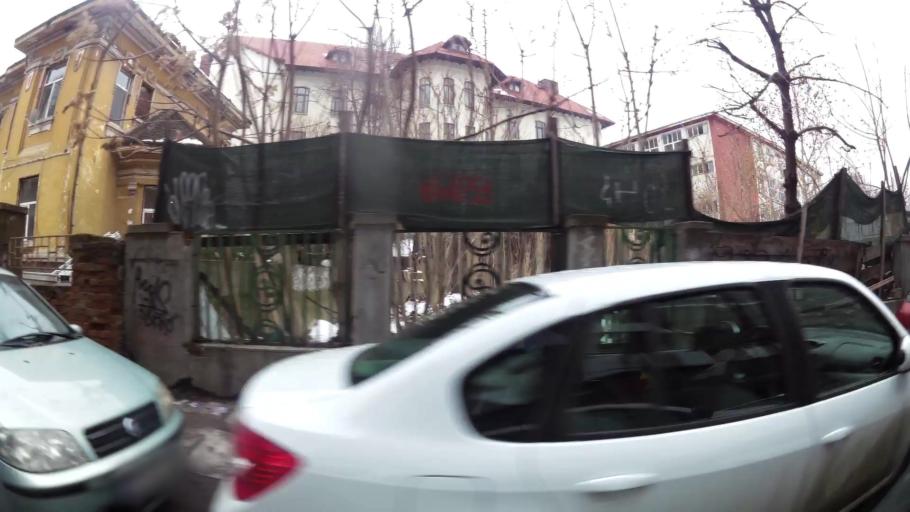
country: RO
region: Bucuresti
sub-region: Municipiul Bucuresti
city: Bucharest
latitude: 44.4378
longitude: 26.1073
